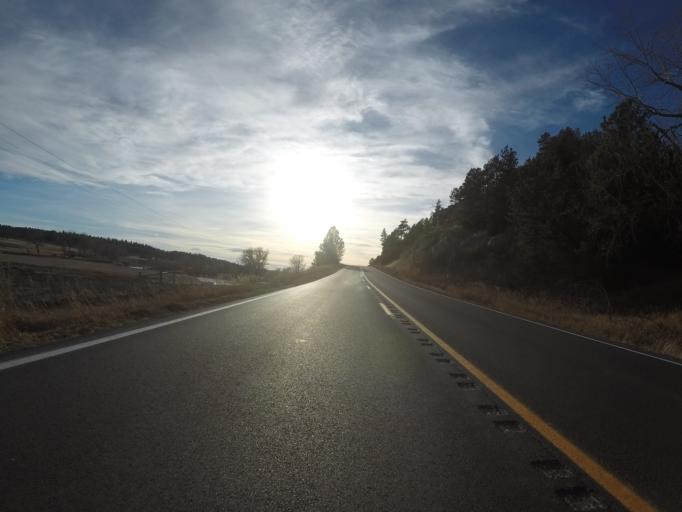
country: US
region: Montana
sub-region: Musselshell County
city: Roundup
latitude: 46.3999
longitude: -108.6029
